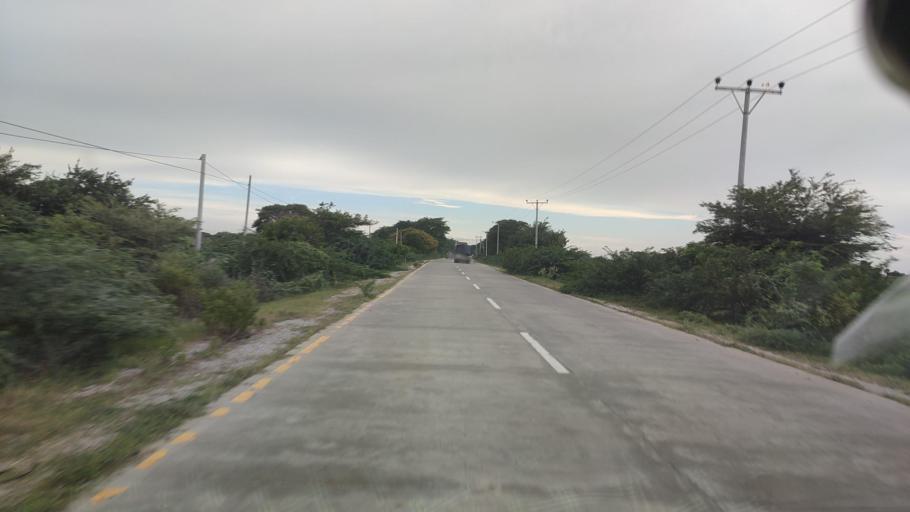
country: MM
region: Mandalay
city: Kyaukse
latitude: 21.3151
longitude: 96.0208
